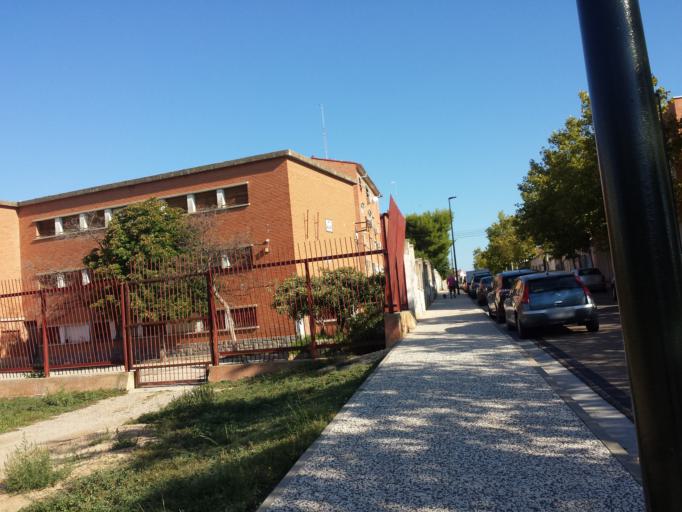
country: ES
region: Aragon
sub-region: Provincia de Zaragoza
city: Oliver-Valdefierro, Oliver, Valdefierro
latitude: 41.6499
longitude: -0.9284
